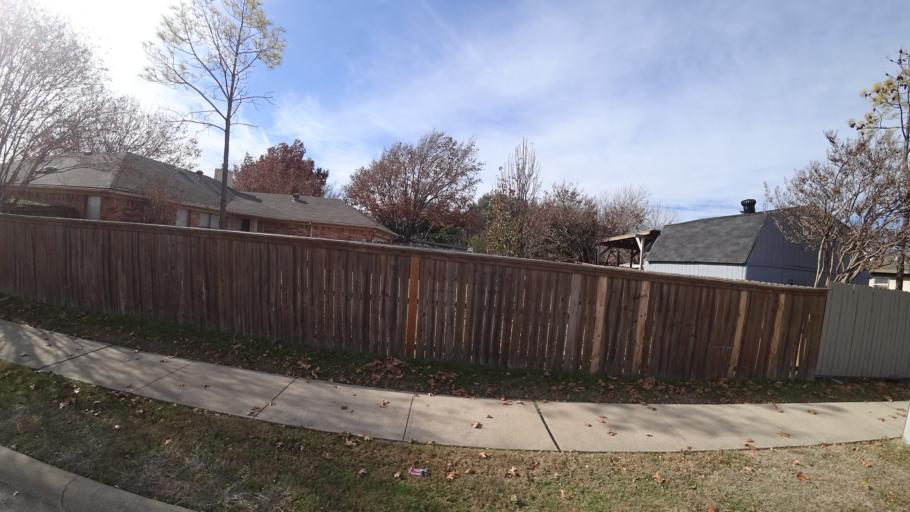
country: US
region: Texas
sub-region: Denton County
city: Highland Village
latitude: 33.0587
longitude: -97.0359
